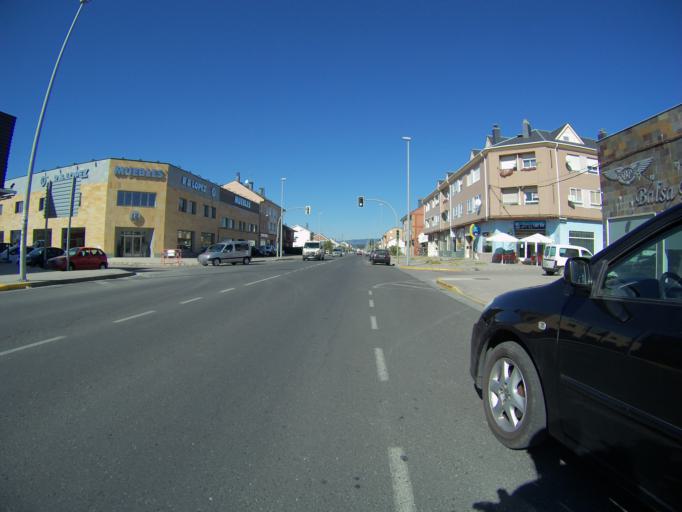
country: ES
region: Castille and Leon
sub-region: Provincia de Leon
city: Camponaraya
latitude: 42.5700
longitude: -6.6469
